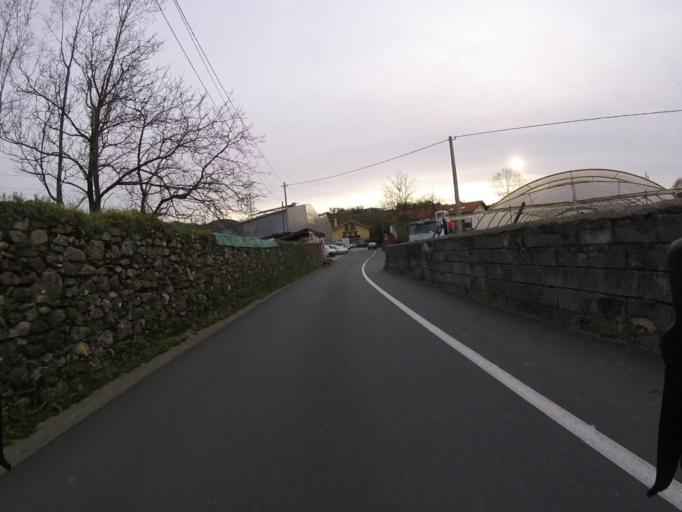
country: ES
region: Basque Country
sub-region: Provincia de Guipuzcoa
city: Errenteria
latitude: 43.2946
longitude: -1.8646
